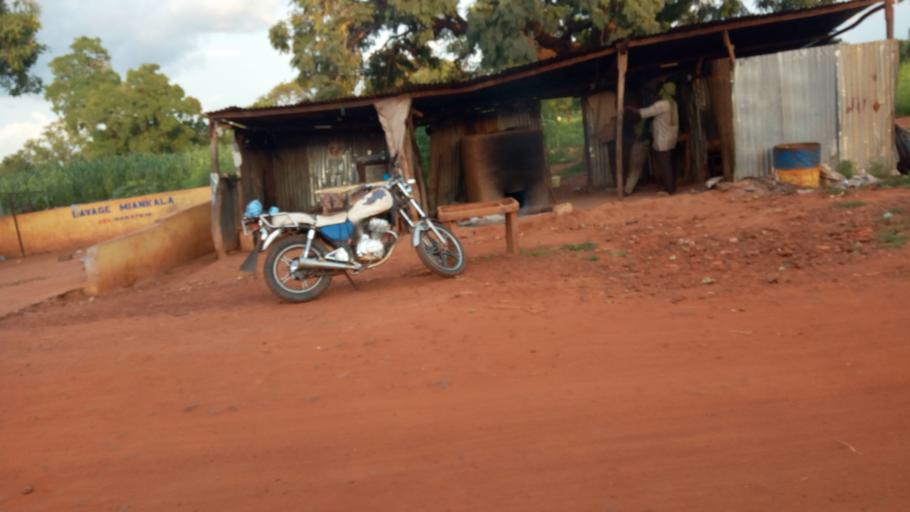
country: ML
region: Sikasso
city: Koutiala
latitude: 12.3719
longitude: -5.4760
